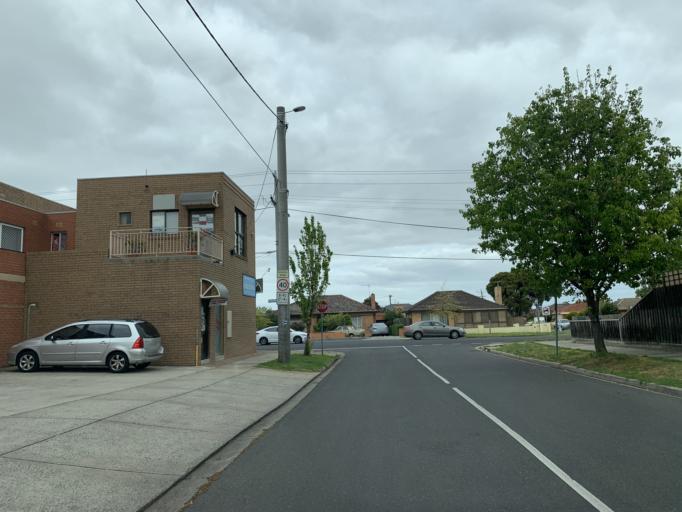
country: AU
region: Victoria
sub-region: Brimbank
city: St Albans
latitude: -37.7451
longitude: 144.8099
